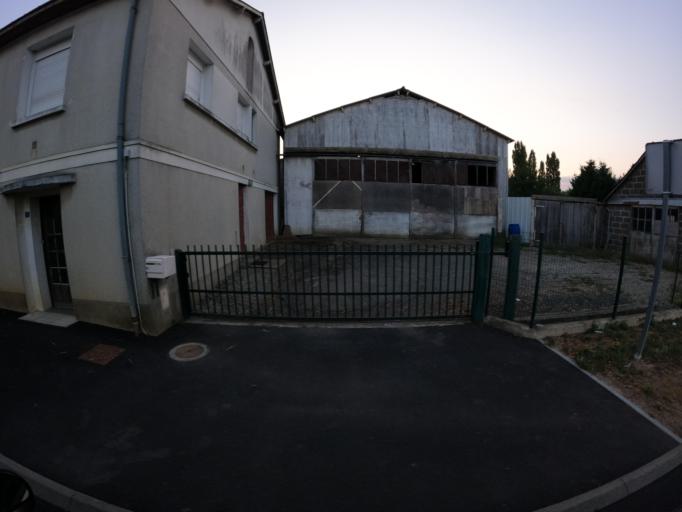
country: FR
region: Pays de la Loire
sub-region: Departement de la Mayenne
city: Chemaze
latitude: 47.7540
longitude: -0.7910
